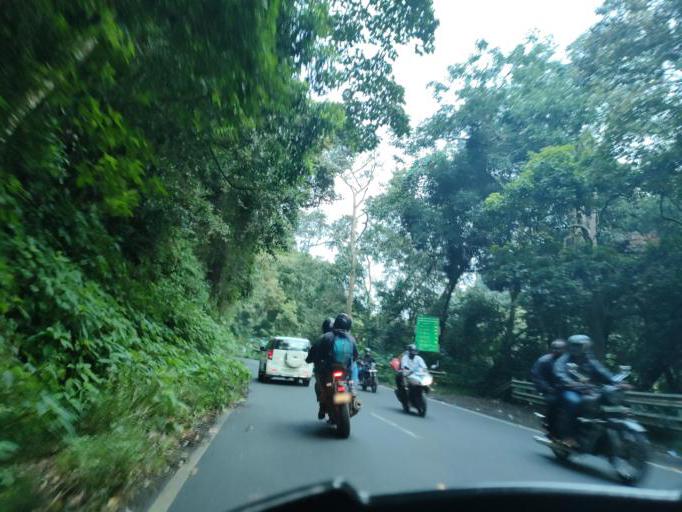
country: IN
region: Tamil Nadu
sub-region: Dindigul
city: Kodaikanal
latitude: 10.2517
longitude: 77.5223
